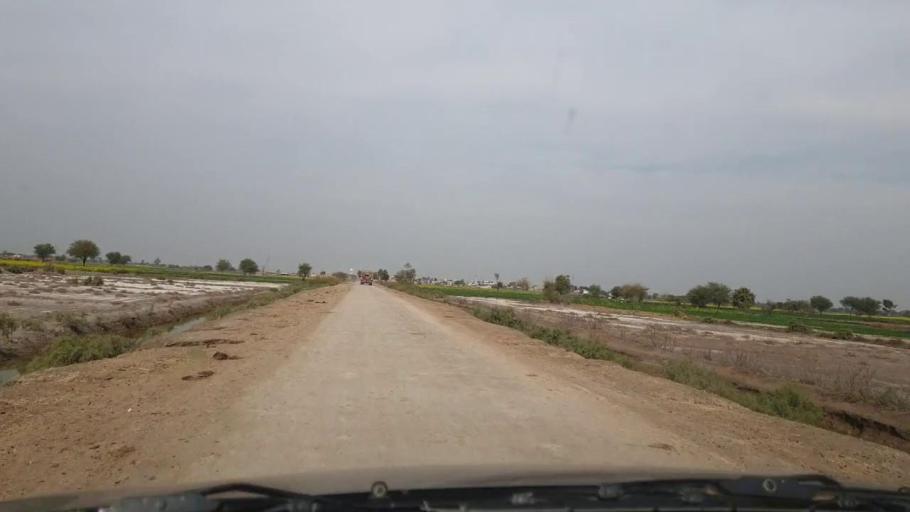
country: PK
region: Sindh
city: Sinjhoro
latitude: 26.0969
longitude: 68.8276
